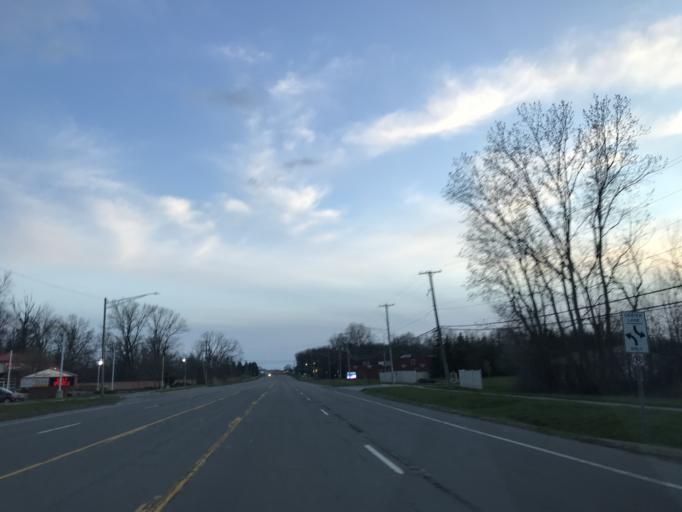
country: US
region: Michigan
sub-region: Wayne County
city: Southgate
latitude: 42.1919
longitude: -83.2194
